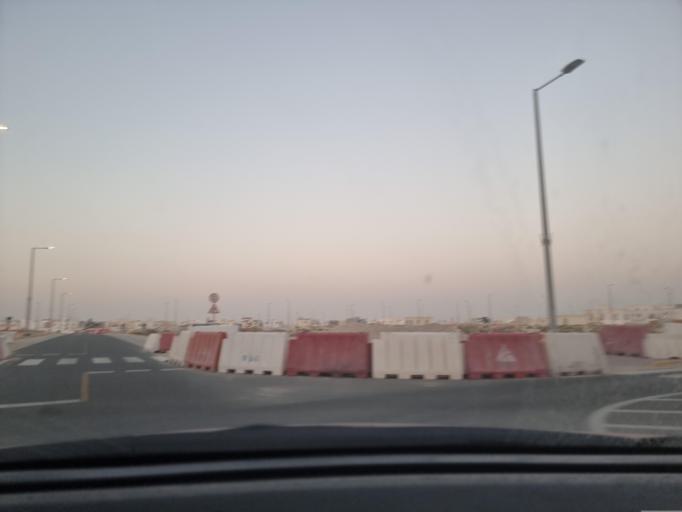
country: AE
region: Abu Dhabi
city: Abu Dhabi
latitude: 24.3681
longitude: 54.7411
